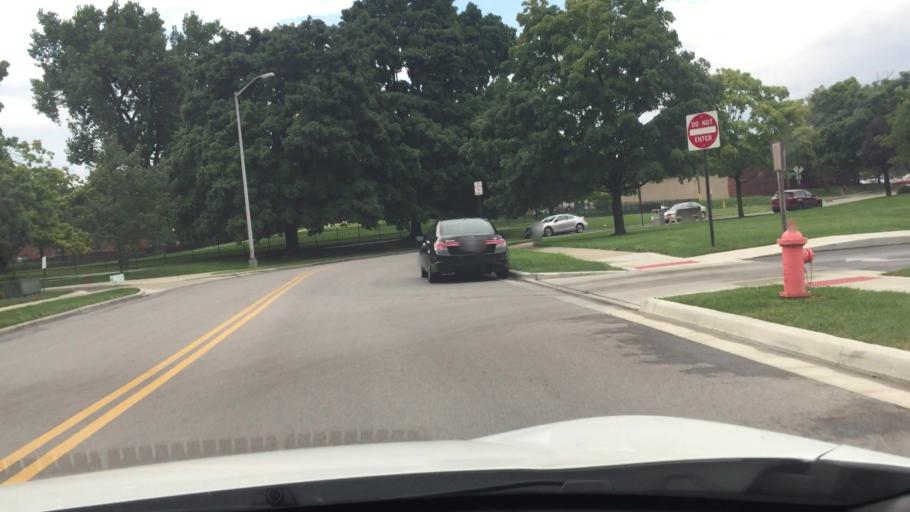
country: US
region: Ohio
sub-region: Franklin County
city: Columbus
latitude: 39.9751
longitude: -83.0131
